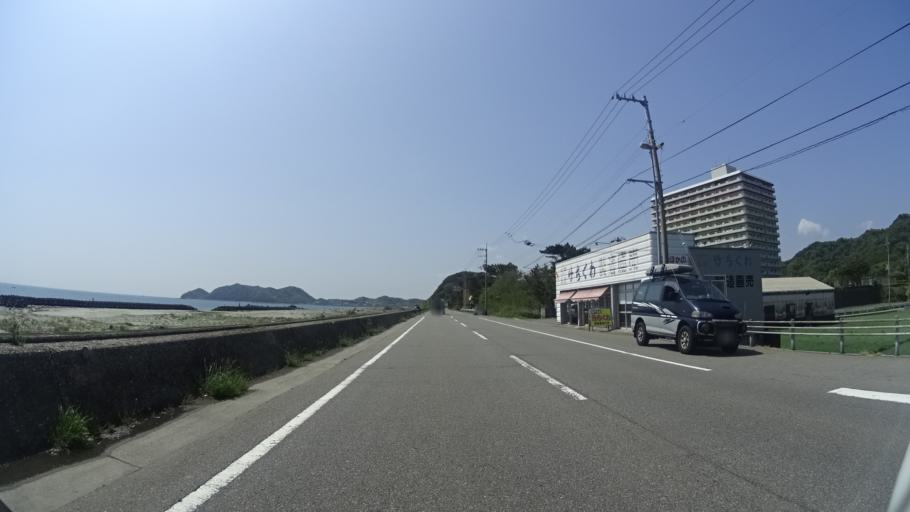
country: JP
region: Tokushima
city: Narutocho-mitsuishi
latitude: 34.1991
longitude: 134.6254
